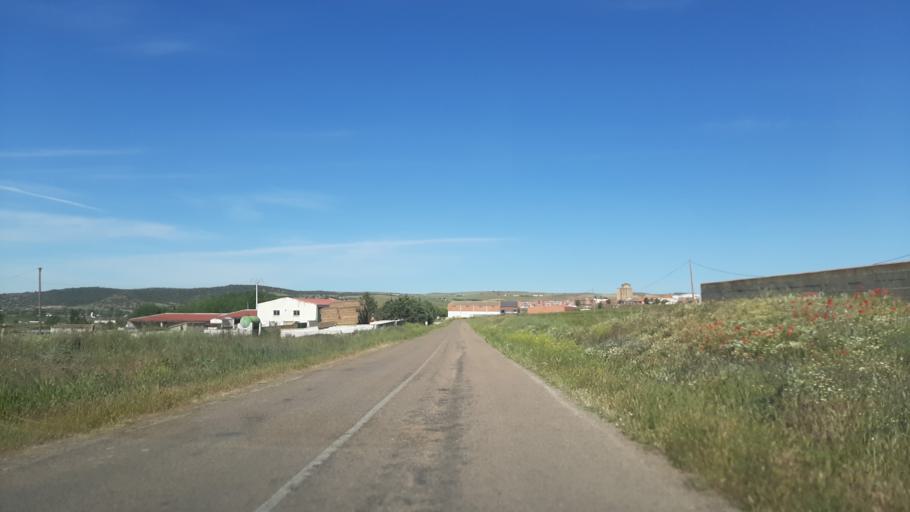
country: ES
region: Castille and Leon
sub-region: Provincia de Salamanca
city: Alba de Tormes
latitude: 40.8204
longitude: -5.4999
